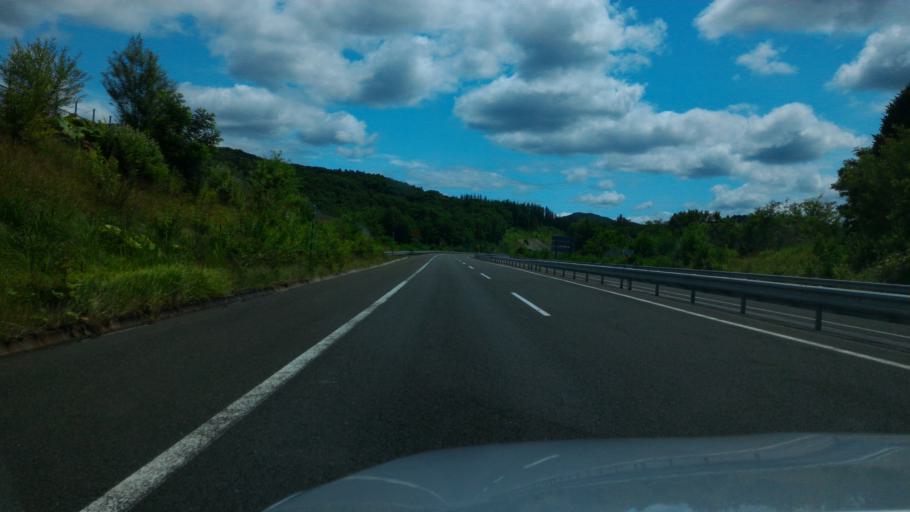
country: JP
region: Hokkaido
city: Shimo-furano
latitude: 42.9906
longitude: 142.4109
